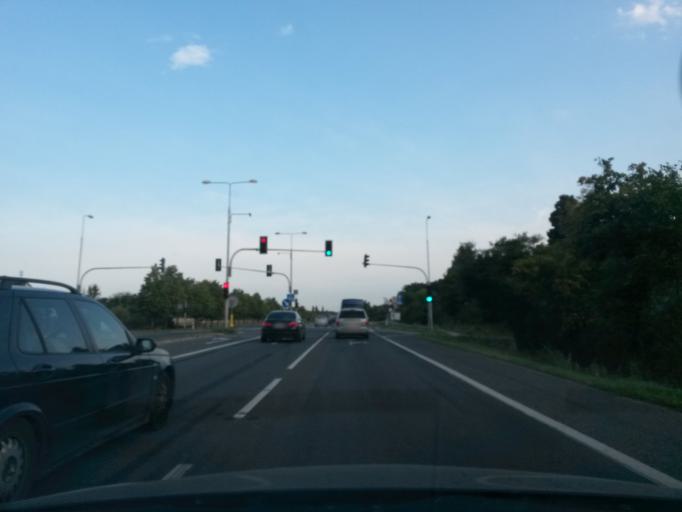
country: PL
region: Masovian Voivodeship
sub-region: Powiat plonski
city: Zaluski
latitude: 52.4986
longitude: 20.5400
